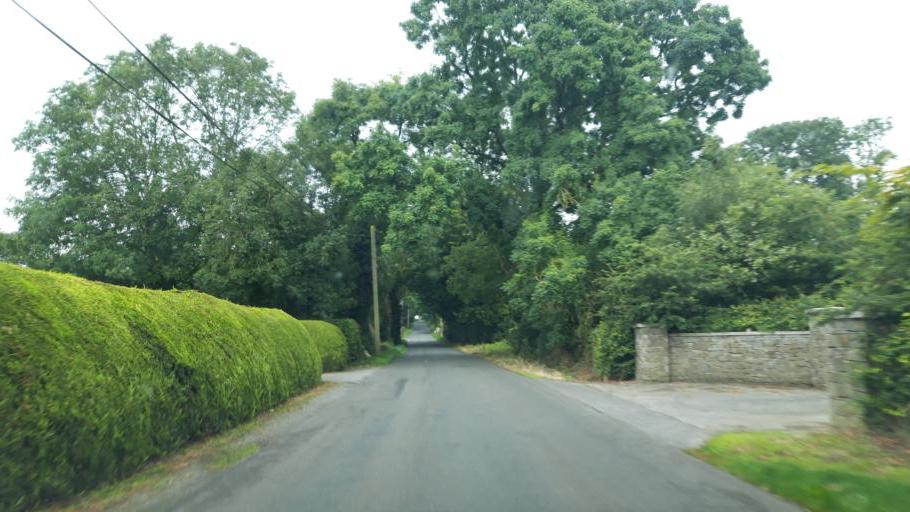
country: IE
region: Leinster
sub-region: Kilkenny
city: Thomastown
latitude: 52.6252
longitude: -7.0769
